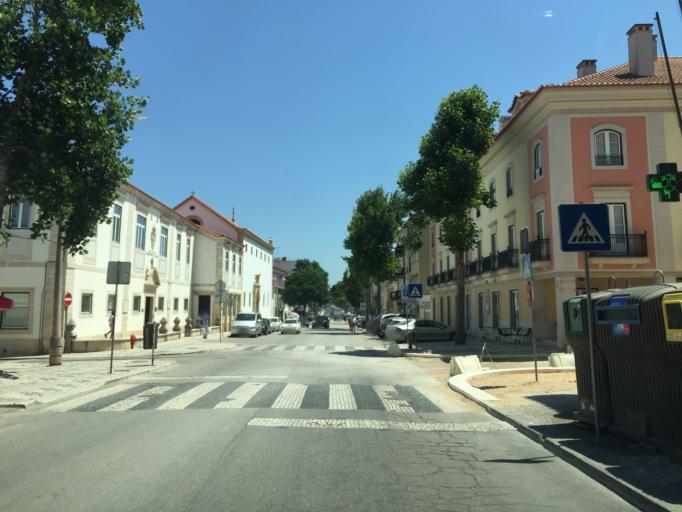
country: PT
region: Santarem
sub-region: Tomar
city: Tomar
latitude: 39.6018
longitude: -8.4148
